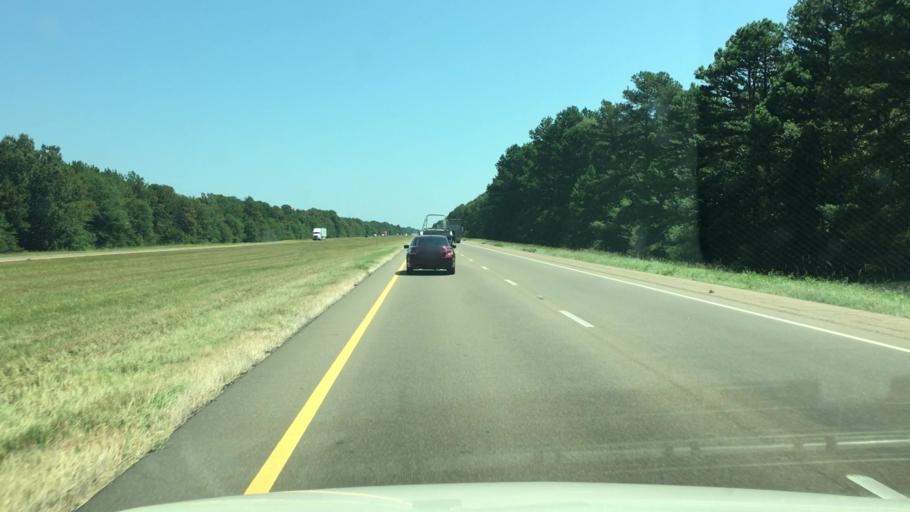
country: US
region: Texas
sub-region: Morris County
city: Naples
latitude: 33.3417
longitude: -94.6609
